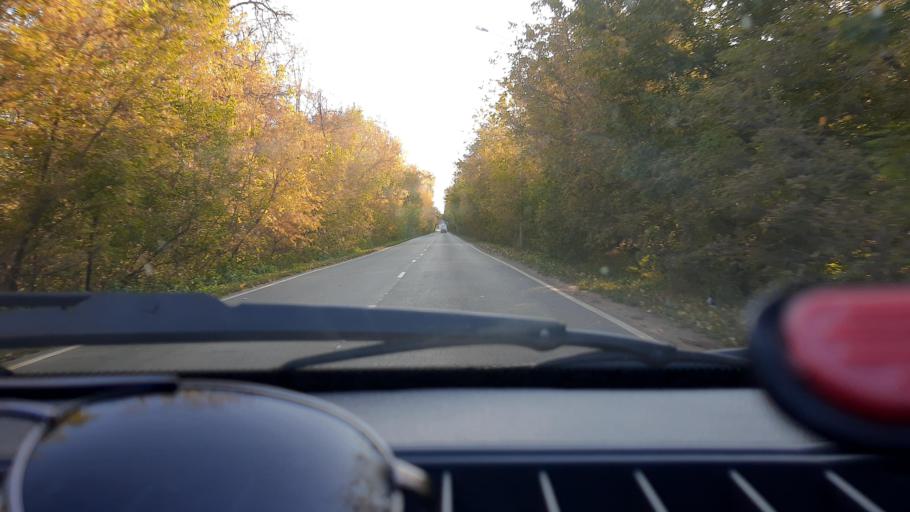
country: RU
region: Bashkortostan
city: Ufa
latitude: 54.6629
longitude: 55.9373
